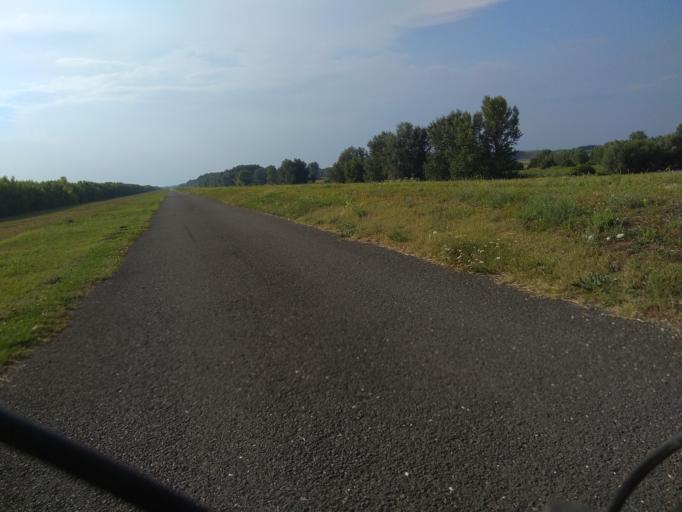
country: SK
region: Trnavsky
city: Gabcikovo
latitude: 47.8394
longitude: 17.5905
